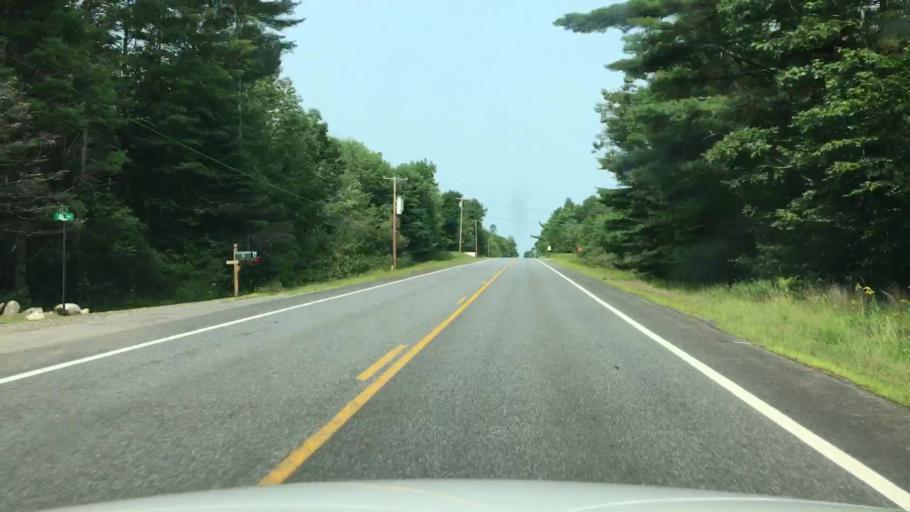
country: US
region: Maine
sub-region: Kennebec County
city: Wayne
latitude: 44.3400
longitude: -70.0221
